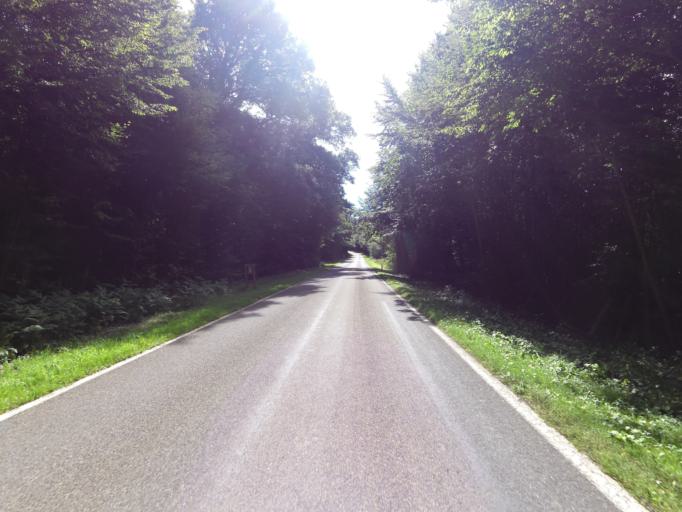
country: BE
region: Wallonia
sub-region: Province du Luxembourg
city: Nassogne
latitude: 50.0802
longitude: 5.3429
